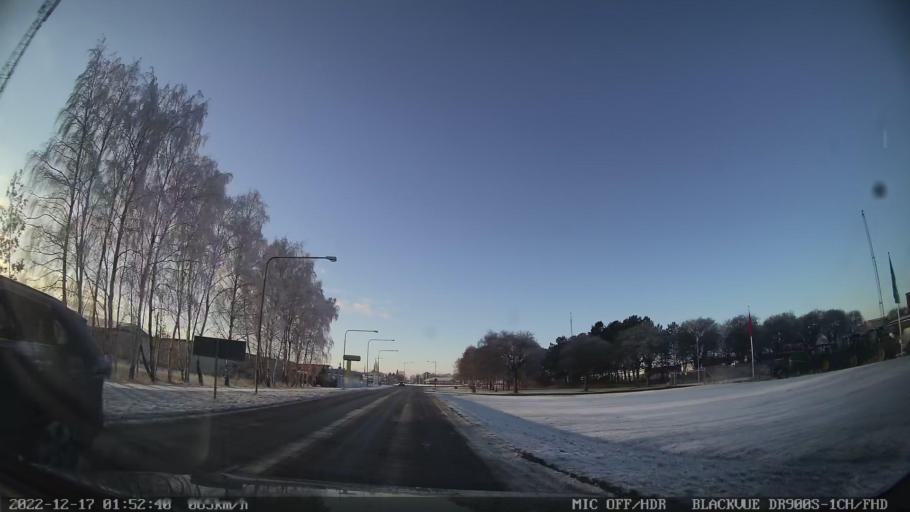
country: SE
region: Skane
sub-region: Tomelilla Kommun
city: Tomelilla
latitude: 55.5454
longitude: 13.9731
